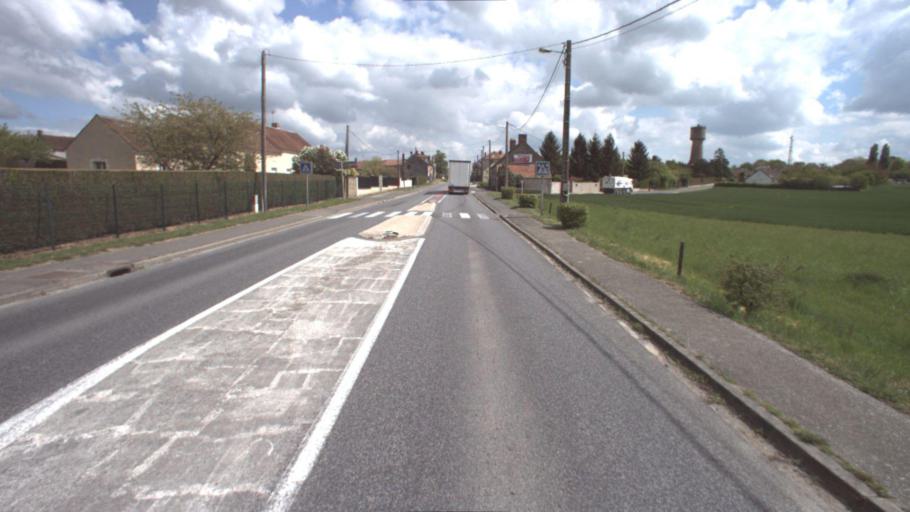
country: FR
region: Ile-de-France
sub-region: Departement de Seine-et-Marne
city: Villiers-Saint-Georges
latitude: 48.6941
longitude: 3.4388
